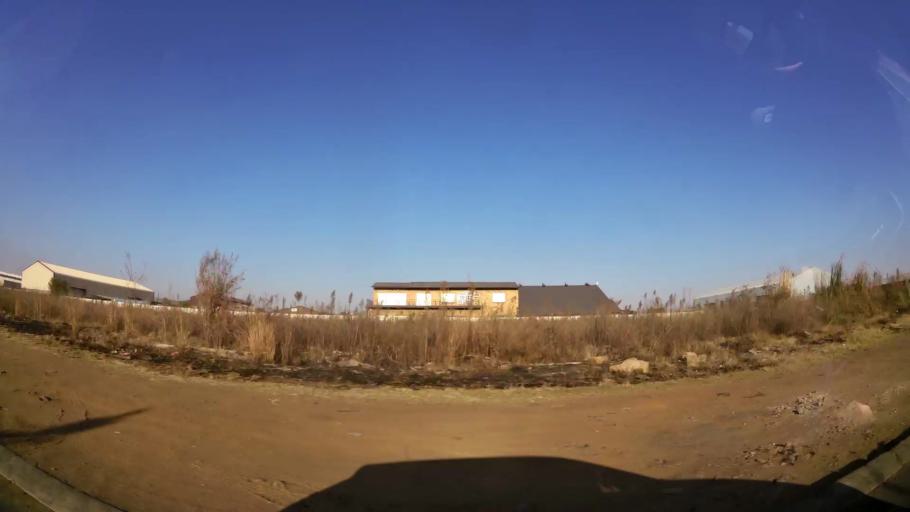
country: ZA
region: Gauteng
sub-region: West Rand District Municipality
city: Randfontein
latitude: -26.1973
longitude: 27.6892
